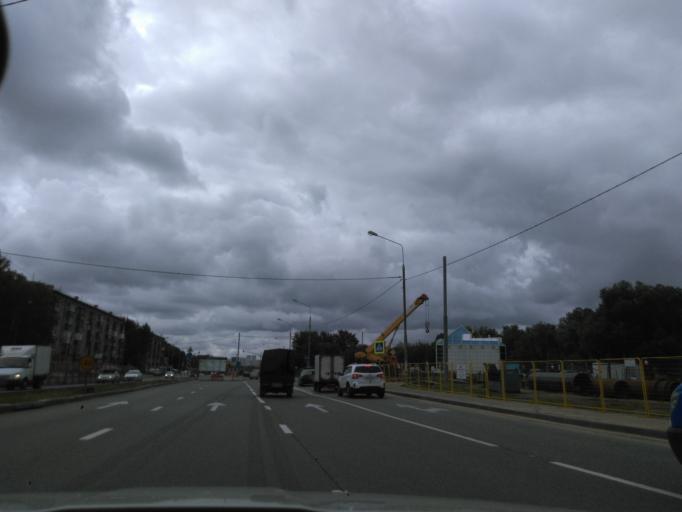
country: RU
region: Moscow
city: Davydkovo
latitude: 55.7201
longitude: 37.4504
